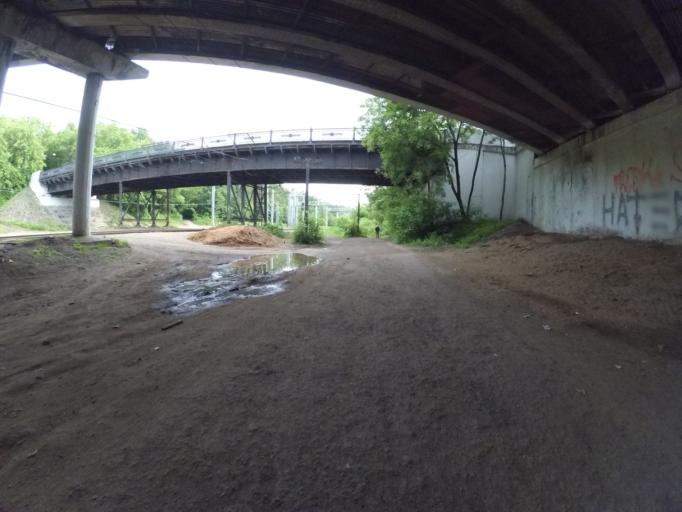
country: RU
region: Moscow
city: Pokrovskoye-Streshnevo
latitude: 55.8135
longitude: 37.4735
